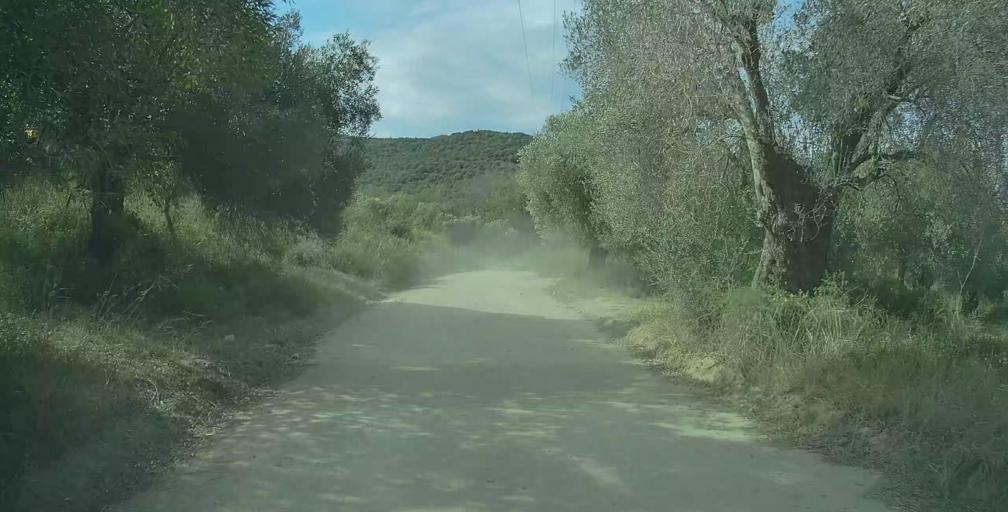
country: GR
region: Central Macedonia
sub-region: Nomos Chalkidikis
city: Sykia
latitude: 40.0295
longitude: 23.9443
